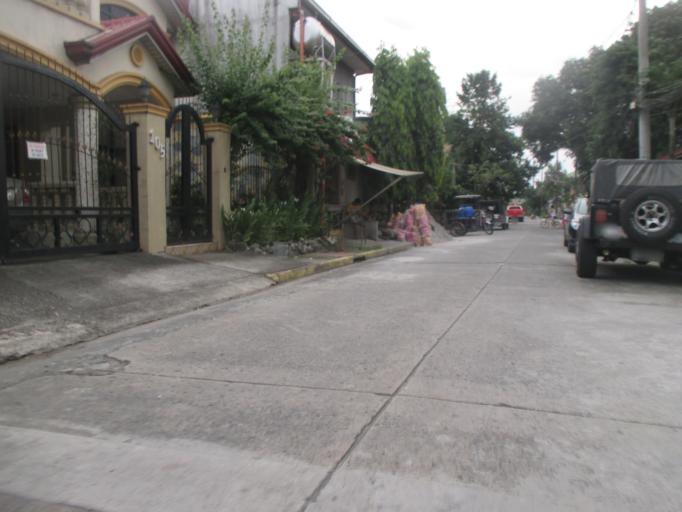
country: PH
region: Metro Manila
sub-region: Marikina
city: Calumpang
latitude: 14.6196
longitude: 121.0895
